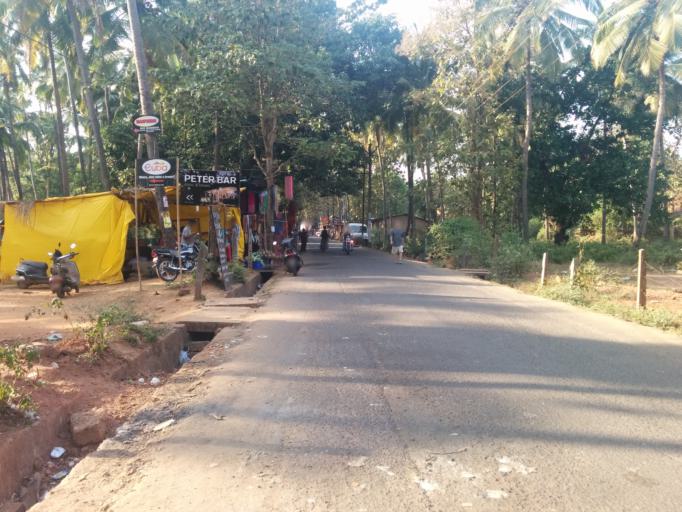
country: IN
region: Goa
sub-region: South Goa
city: Kankon
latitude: 15.0112
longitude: 74.0256
